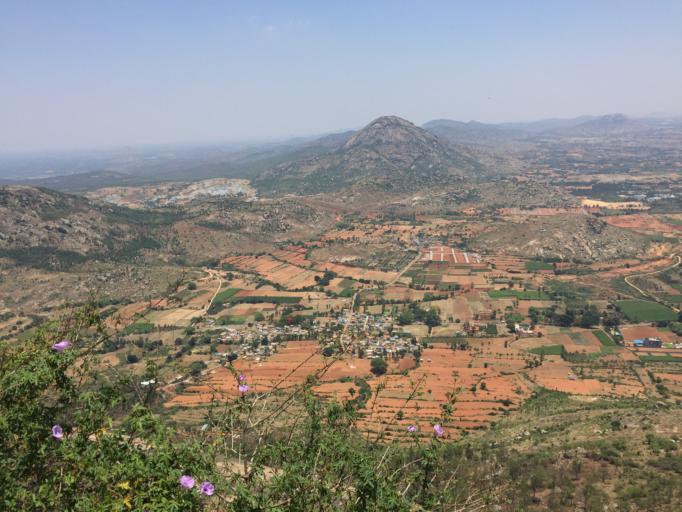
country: IN
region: Karnataka
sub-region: Chikkaballapur
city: Chik Ballapur
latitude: 13.3719
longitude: 77.6868
